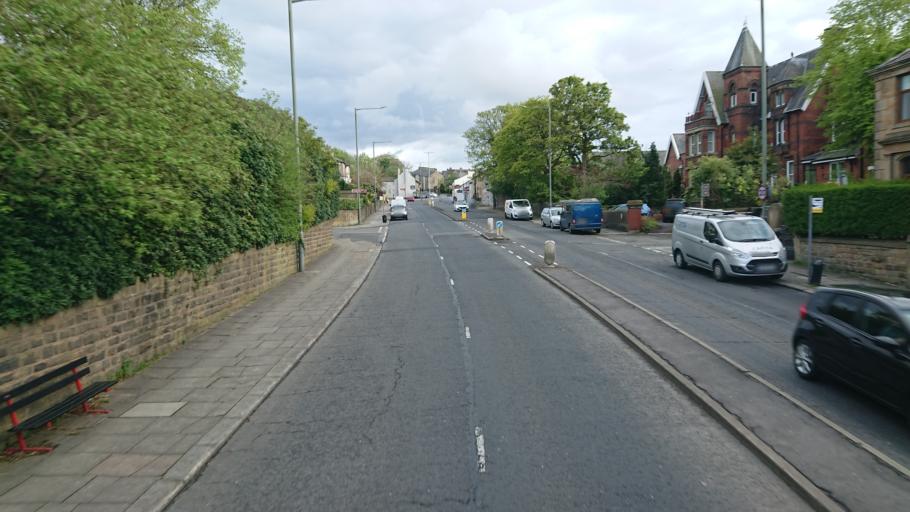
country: GB
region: England
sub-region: Lancashire
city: Burnley
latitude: 53.7796
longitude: -2.2543
